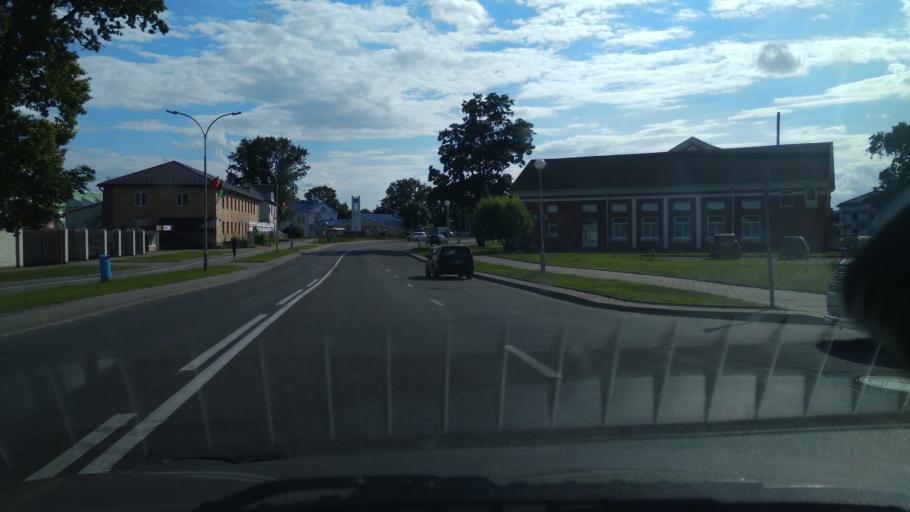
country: BY
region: Grodnenskaya
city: Masty
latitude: 53.4084
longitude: 24.5370
